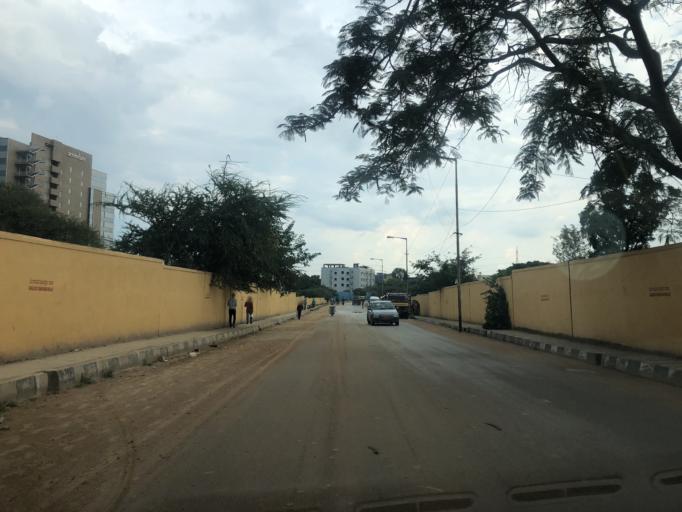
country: IN
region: Karnataka
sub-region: Bangalore Urban
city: Bangalore
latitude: 12.9846
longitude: 77.6977
